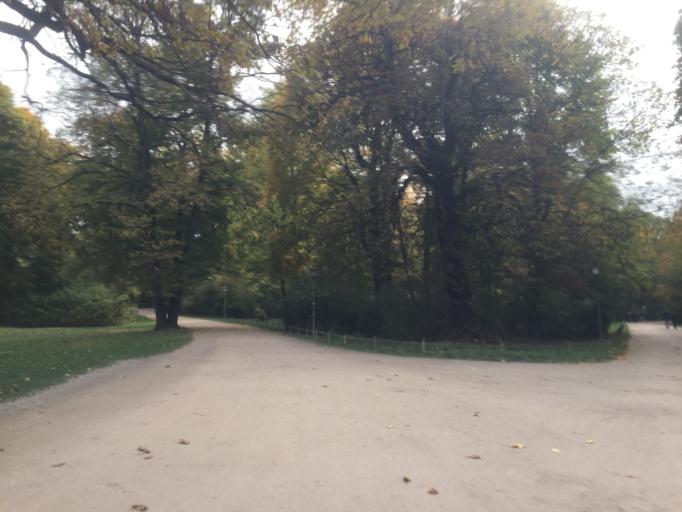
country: DE
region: Bavaria
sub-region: Upper Bavaria
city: Munich
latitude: 48.1481
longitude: 11.5907
